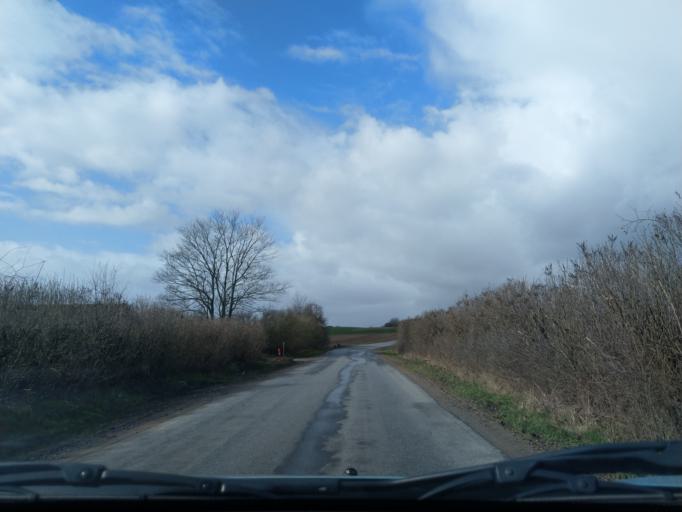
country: DK
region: Zealand
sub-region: Naestved Kommune
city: Fuglebjerg
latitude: 55.3183
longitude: 11.6463
